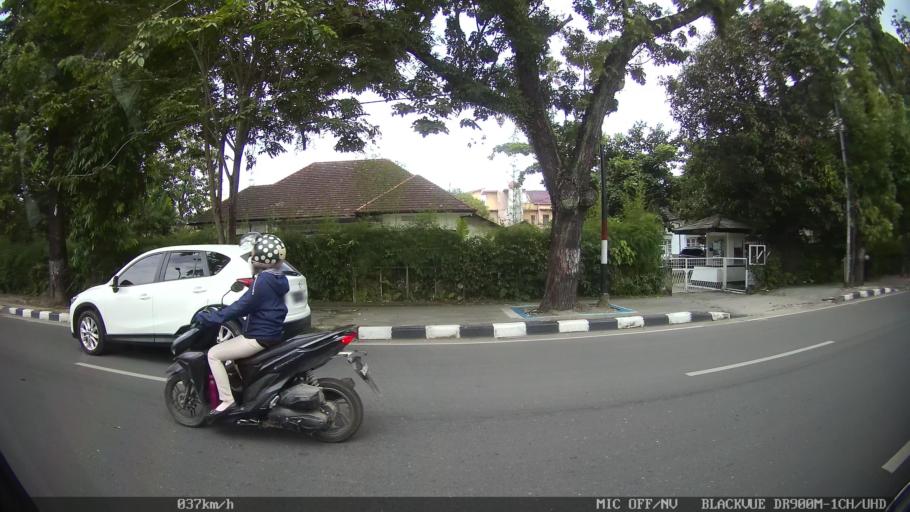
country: ID
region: North Sumatra
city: Medan
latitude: 3.5785
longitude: 98.6726
